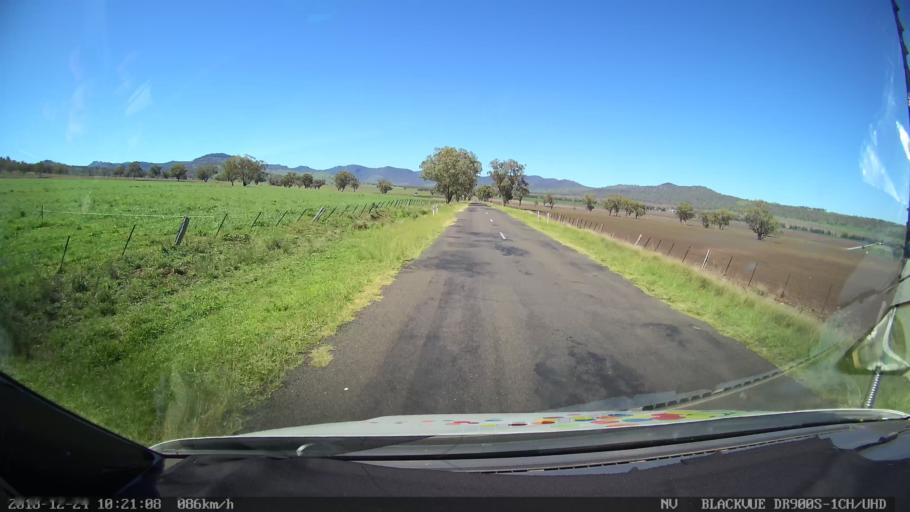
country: AU
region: New South Wales
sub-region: Liverpool Plains
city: Quirindi
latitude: -31.7488
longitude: 150.5527
